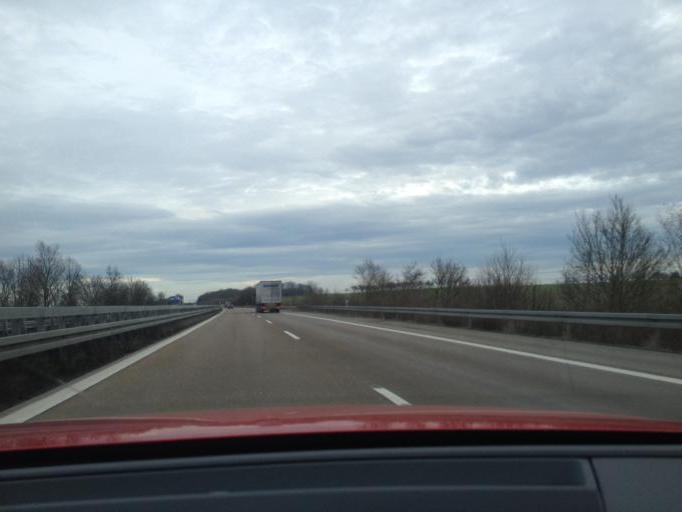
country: DE
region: Baden-Wuerttemberg
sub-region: Regierungsbezirk Stuttgart
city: Wolpertshausen
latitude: 49.1727
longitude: 9.8199
